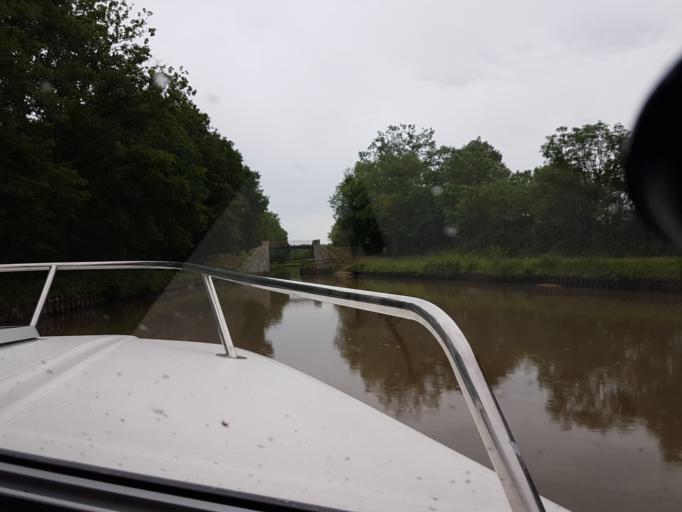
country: FR
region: Bourgogne
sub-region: Departement de la Nievre
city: Clamecy
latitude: 47.3694
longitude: 3.6104
